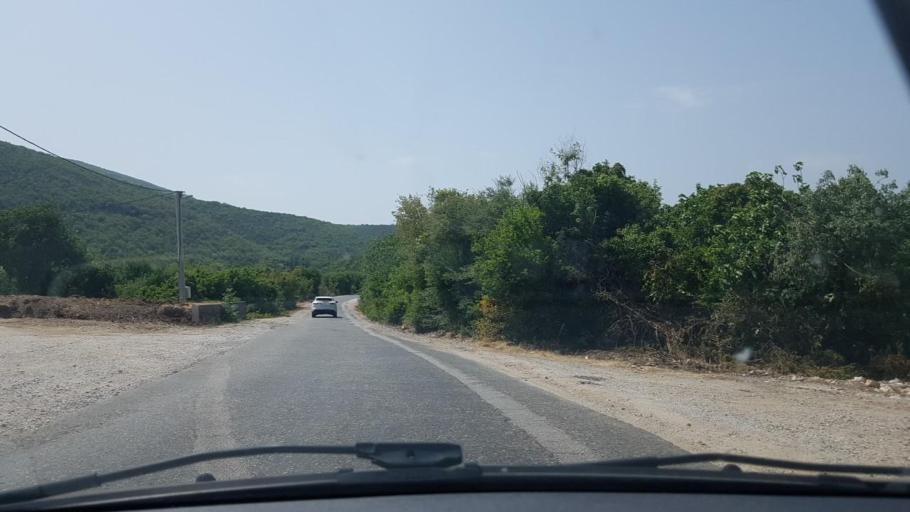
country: BA
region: Federation of Bosnia and Herzegovina
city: Tasovcici
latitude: 43.0222
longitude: 17.7617
